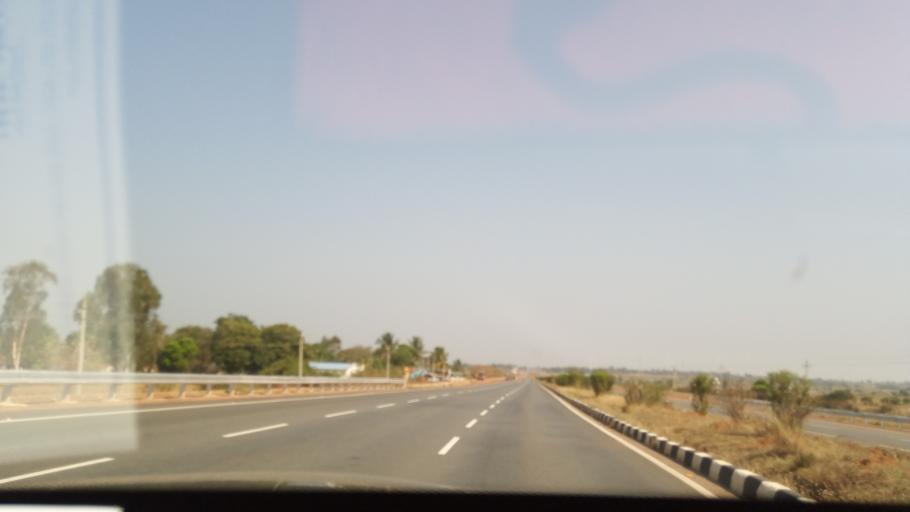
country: IN
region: Karnataka
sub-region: Haveri
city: Shiggaon
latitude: 15.0820
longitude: 75.1519
